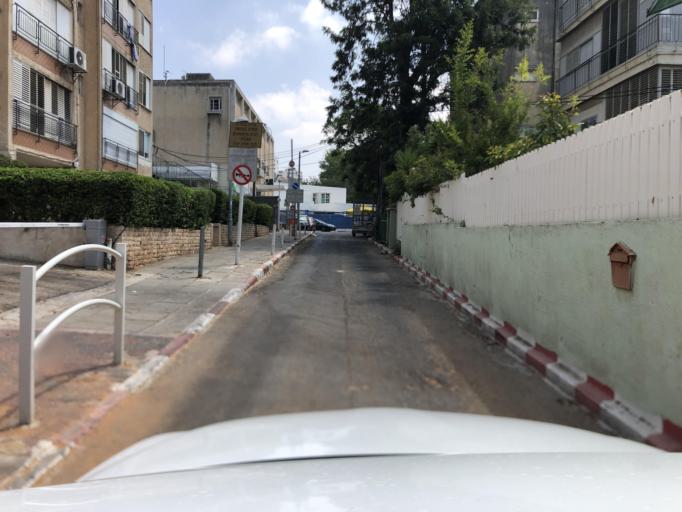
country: IL
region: Tel Aviv
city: Giv`atayim
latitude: 32.0762
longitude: 34.8093
